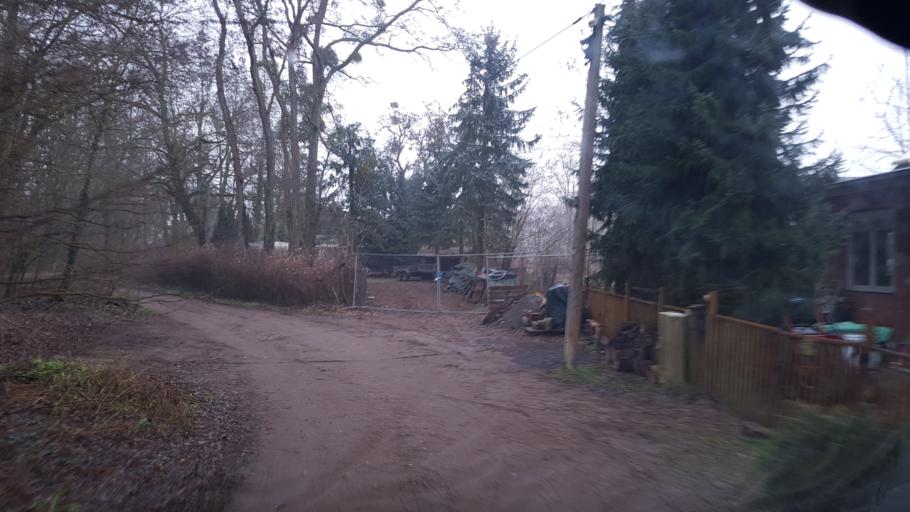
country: DE
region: Brandenburg
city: Stahnsdorf
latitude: 52.3600
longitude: 13.1934
